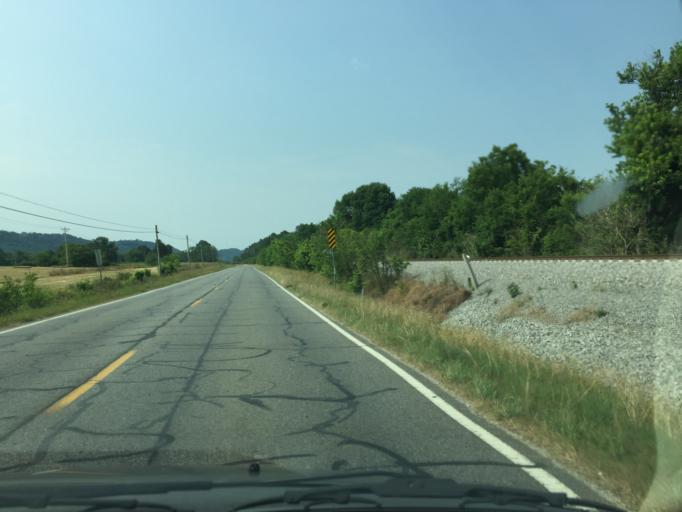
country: US
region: Georgia
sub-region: Catoosa County
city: Ringgold
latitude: 34.9491
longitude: -85.1042
